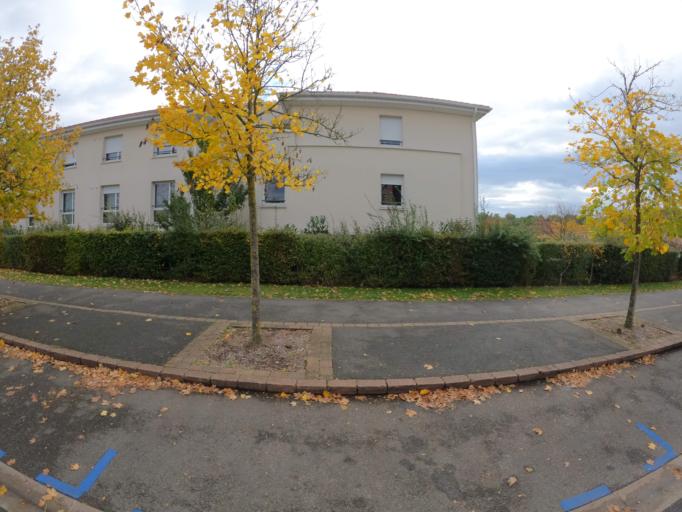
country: FR
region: Ile-de-France
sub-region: Departement de Seine-et-Marne
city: Magny-le-Hongre
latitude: 48.8678
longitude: 2.8148
